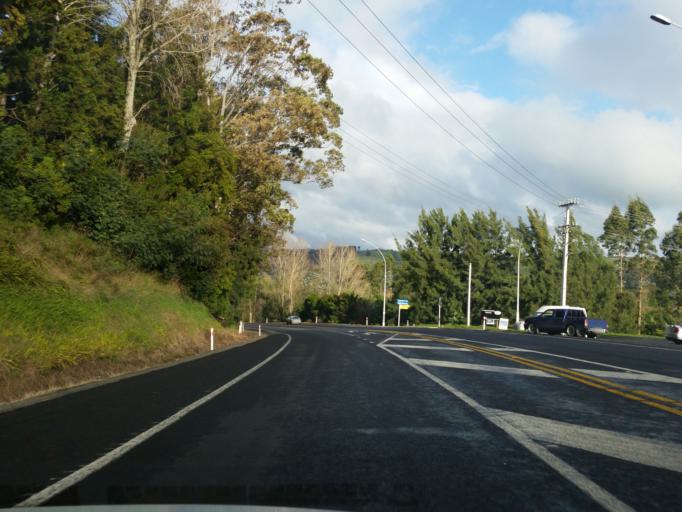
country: NZ
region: Bay of Plenty
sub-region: Tauranga City
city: Tauranga
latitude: -37.6809
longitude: 176.0254
